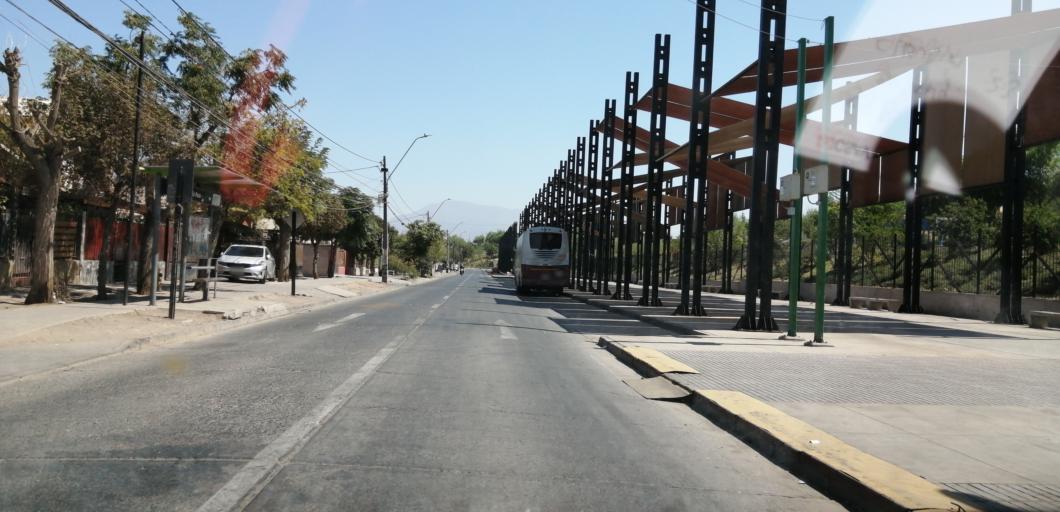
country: CL
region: Santiago Metropolitan
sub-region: Provincia de Santiago
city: Lo Prado
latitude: -33.4477
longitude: -70.7472
